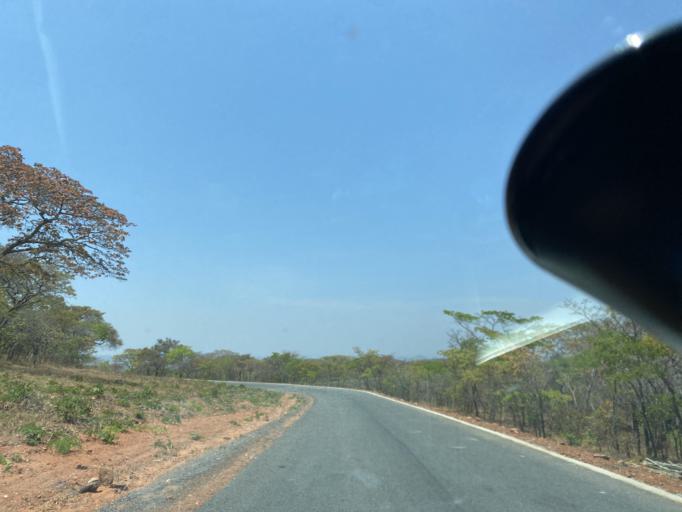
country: ZM
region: Lusaka
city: Kafue
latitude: -15.8574
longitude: 28.4192
